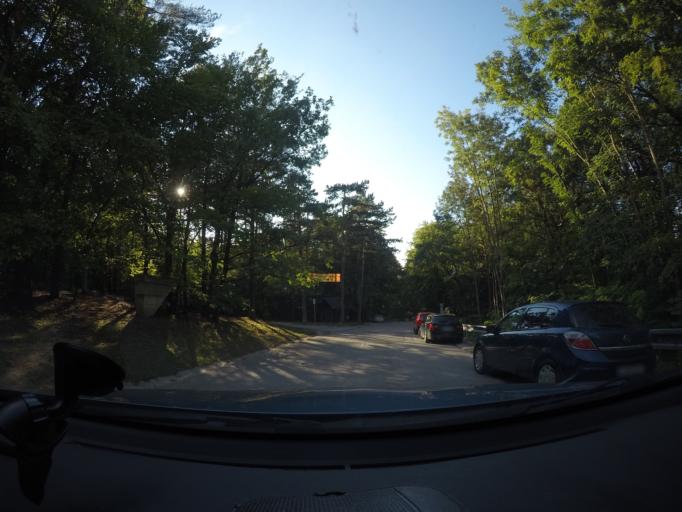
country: SK
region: Trenciansky
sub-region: Okres Trencin
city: Trencin
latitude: 48.8833
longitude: 18.0485
